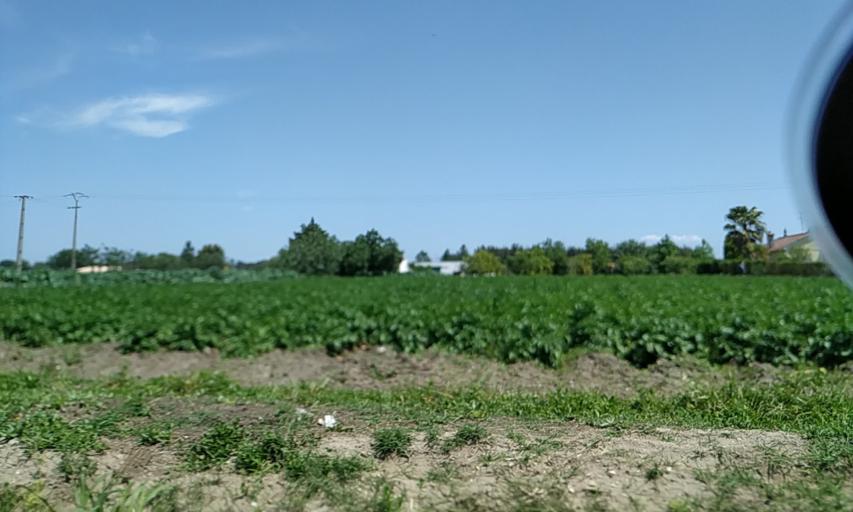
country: PT
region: Santarem
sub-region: Benavente
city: Poceirao
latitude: 38.6715
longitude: -8.7355
